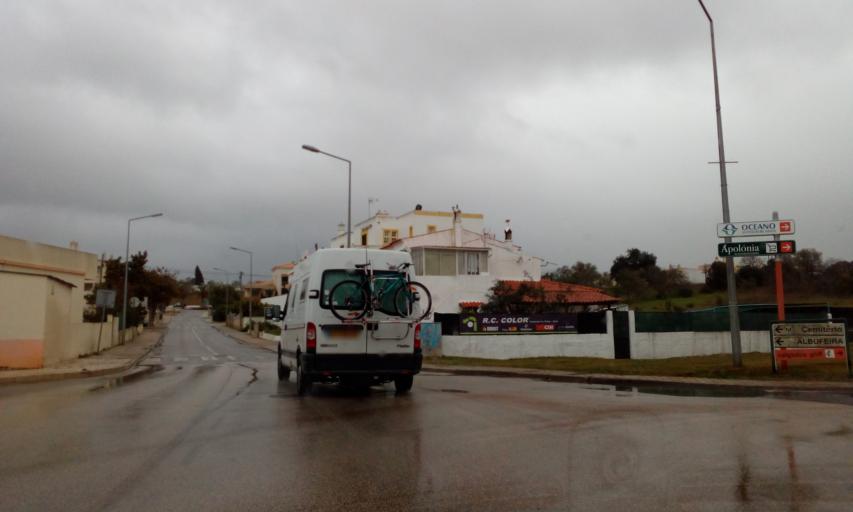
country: PT
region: Faro
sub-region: Albufeira
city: Guia
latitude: 37.1244
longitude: -8.3000
